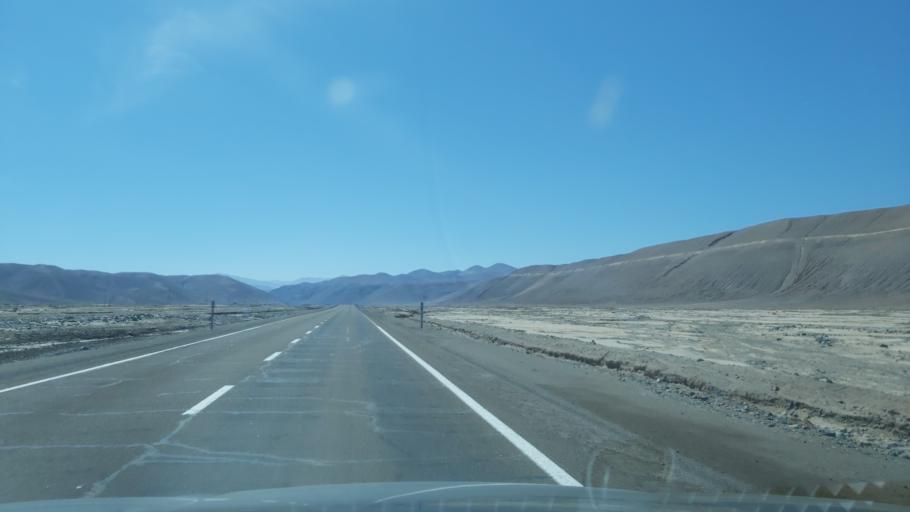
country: CL
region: Atacama
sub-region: Provincia de Chanaral
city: Diego de Almagro
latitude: -26.3529
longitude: -69.9028
